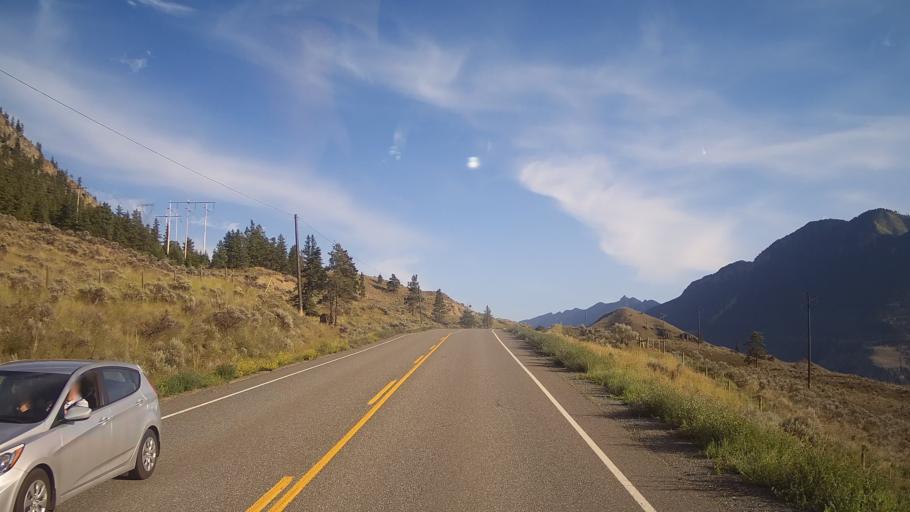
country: CA
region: British Columbia
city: Lillooet
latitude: 50.8320
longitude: -121.8601
